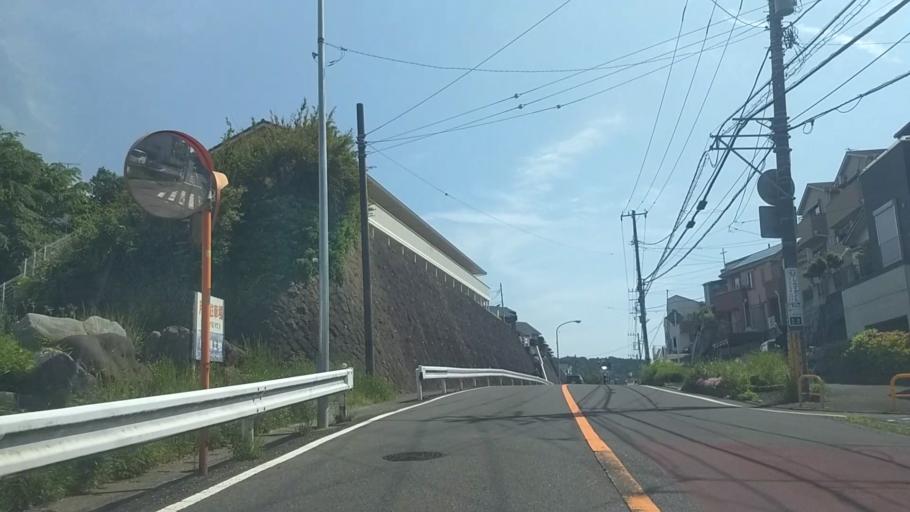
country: JP
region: Kanagawa
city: Kamakura
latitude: 35.3487
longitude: 139.5428
